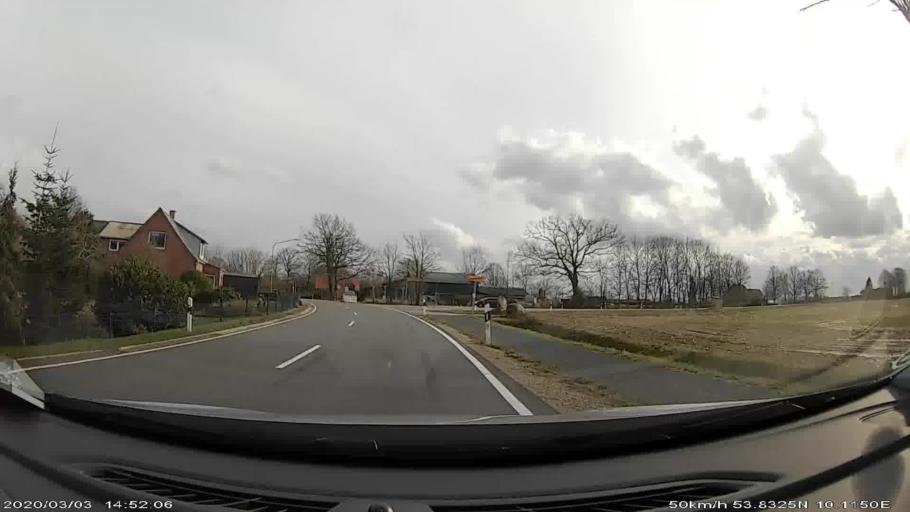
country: DE
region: Schleswig-Holstein
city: Sievershutten
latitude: 53.8327
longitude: 10.1150
